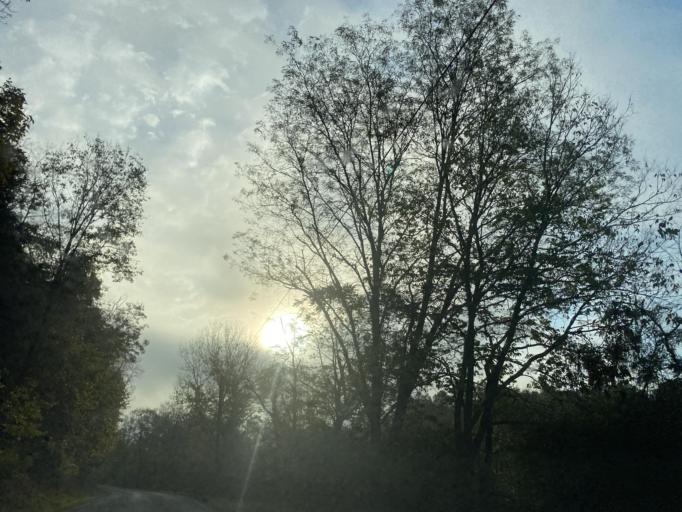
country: US
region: Kentucky
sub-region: Pendleton County
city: Falmouth
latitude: 38.7258
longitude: -84.3184
